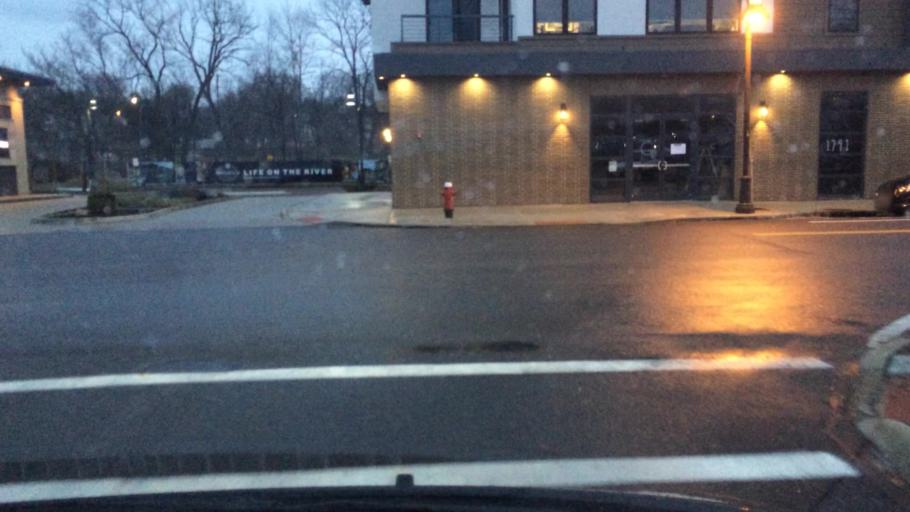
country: US
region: Ohio
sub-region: Summit County
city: Cuyahoga Falls
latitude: 41.1296
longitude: -81.4845
